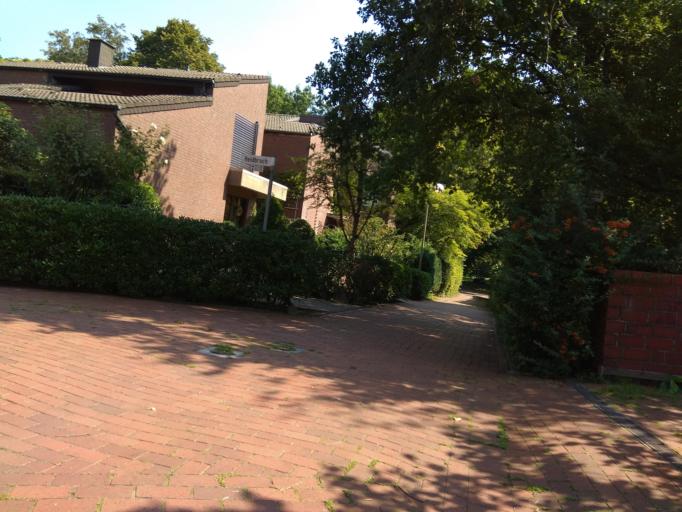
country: DE
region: North Rhine-Westphalia
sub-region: Regierungsbezirk Munster
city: Klein Reken
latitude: 51.7271
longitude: 7.0224
